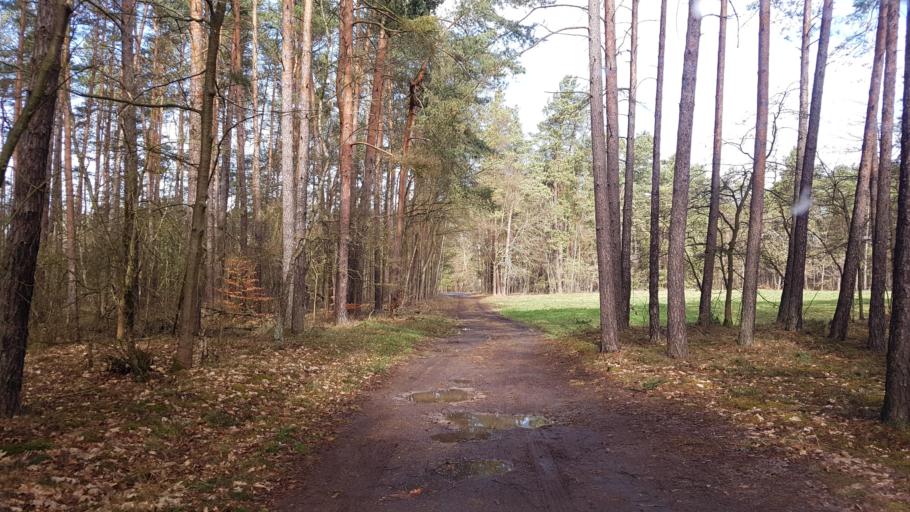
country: DE
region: Brandenburg
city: Altdobern
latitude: 51.6980
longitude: 14.0371
